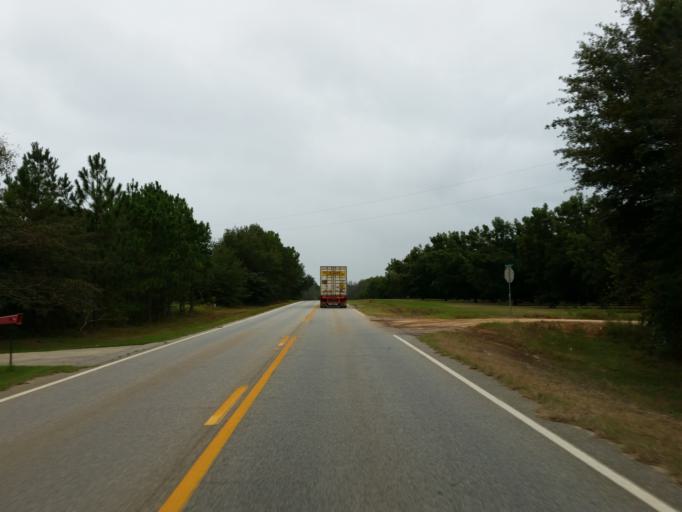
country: US
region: Georgia
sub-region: Berrien County
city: Ray City
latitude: 31.0872
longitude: -83.2416
